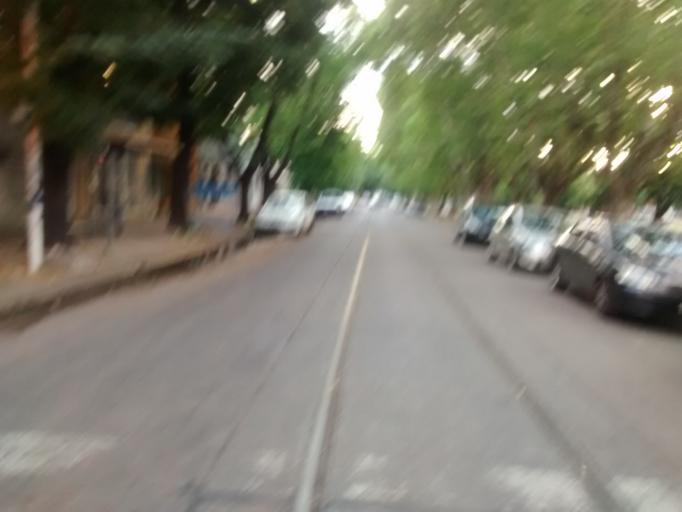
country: AR
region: Buenos Aires
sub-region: Partido de La Plata
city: La Plata
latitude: -34.9280
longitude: -57.9596
